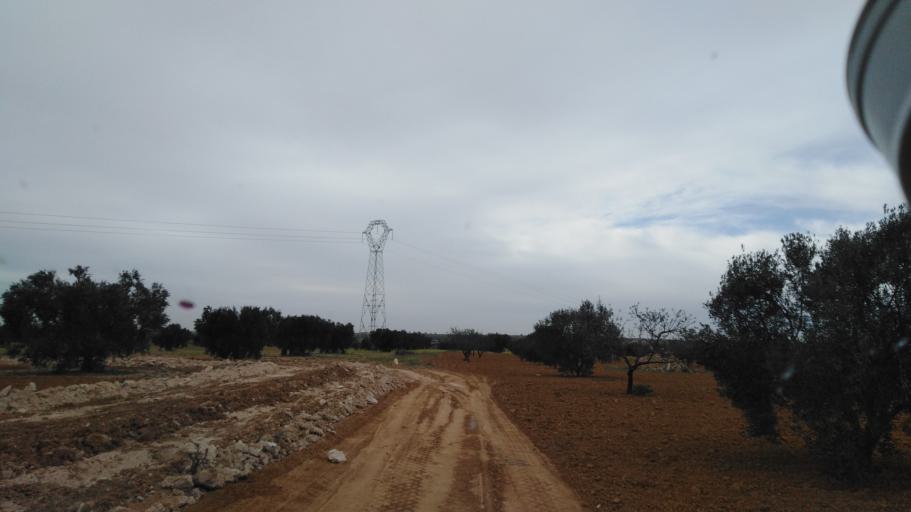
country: TN
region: Safaqis
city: Bi'r `Ali Bin Khalifah
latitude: 34.7710
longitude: 10.3736
